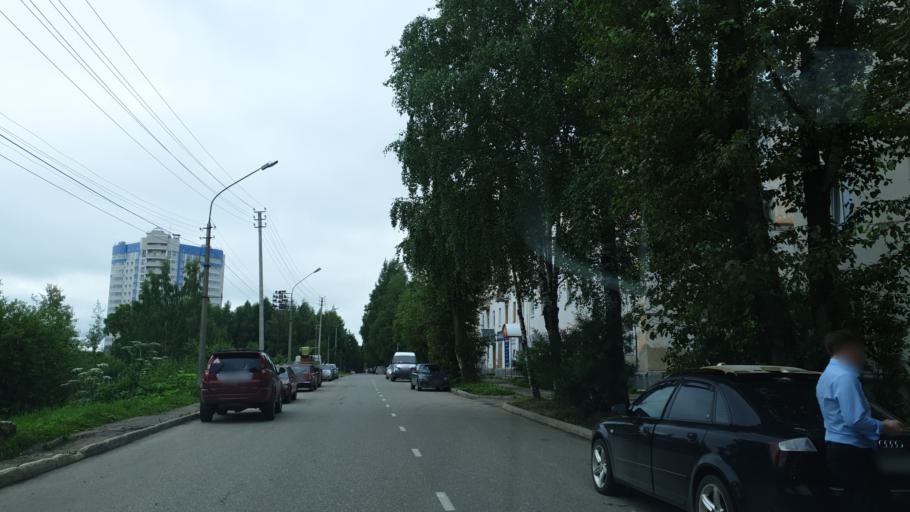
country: RU
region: Komi Republic
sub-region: Syktyvdinskiy Rayon
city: Syktyvkar
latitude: 61.6634
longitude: 50.8250
